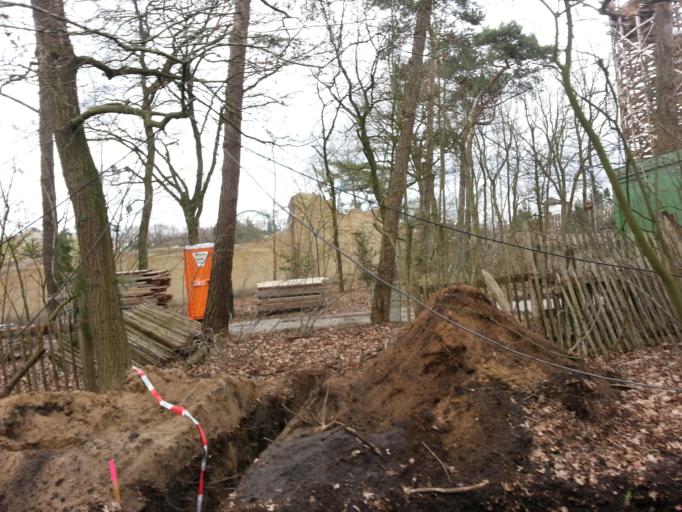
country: NL
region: North Brabant
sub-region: Gemeente Loon op Zand
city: Loon op Zand
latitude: 51.6462
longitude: 5.0507
